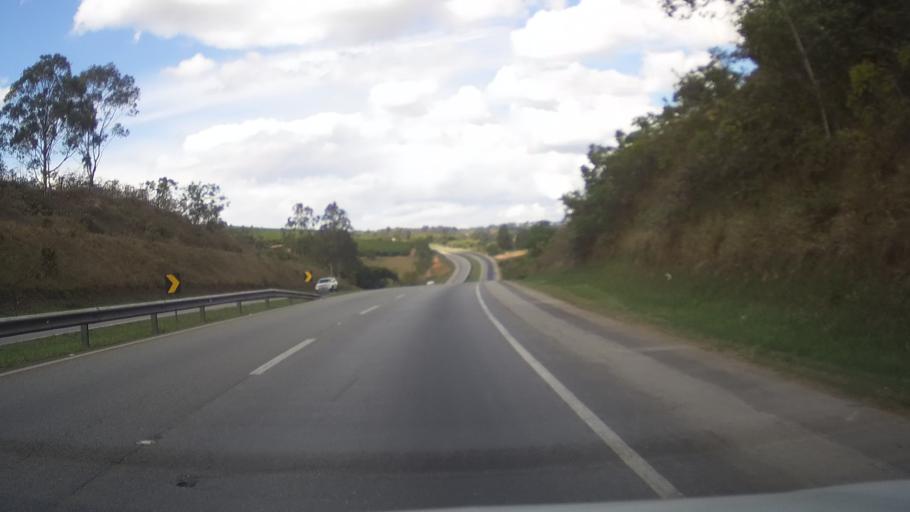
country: BR
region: Minas Gerais
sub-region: Santo Antonio Do Amparo
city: Santo Antonio do Amparo
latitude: -20.8469
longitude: -44.8324
